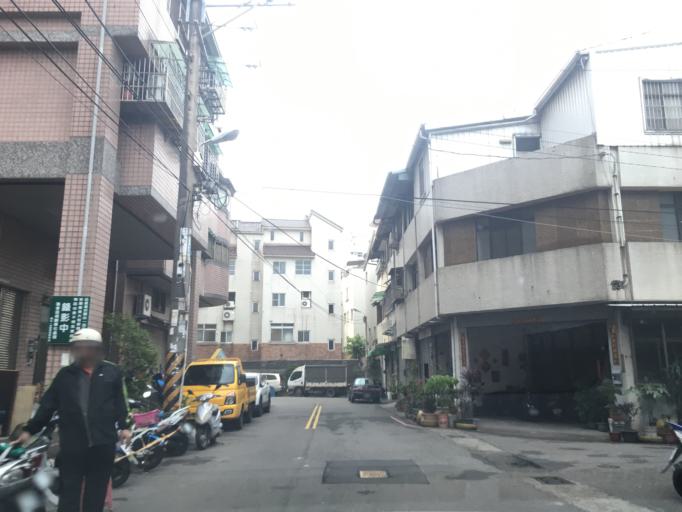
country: TW
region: Taiwan
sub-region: Taichung City
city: Taichung
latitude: 24.1881
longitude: 120.7004
